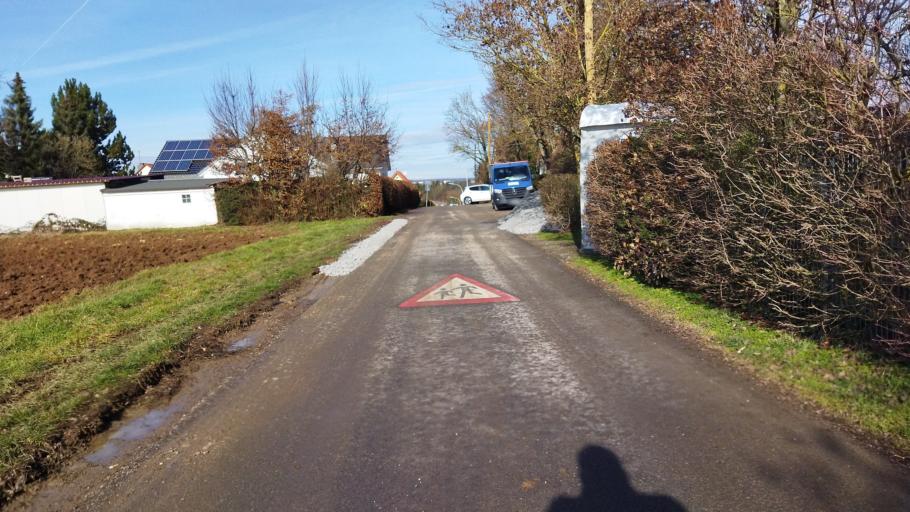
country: DE
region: Baden-Wuerttemberg
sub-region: Regierungsbezirk Stuttgart
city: Heilbronn
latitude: 49.1367
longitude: 9.1762
